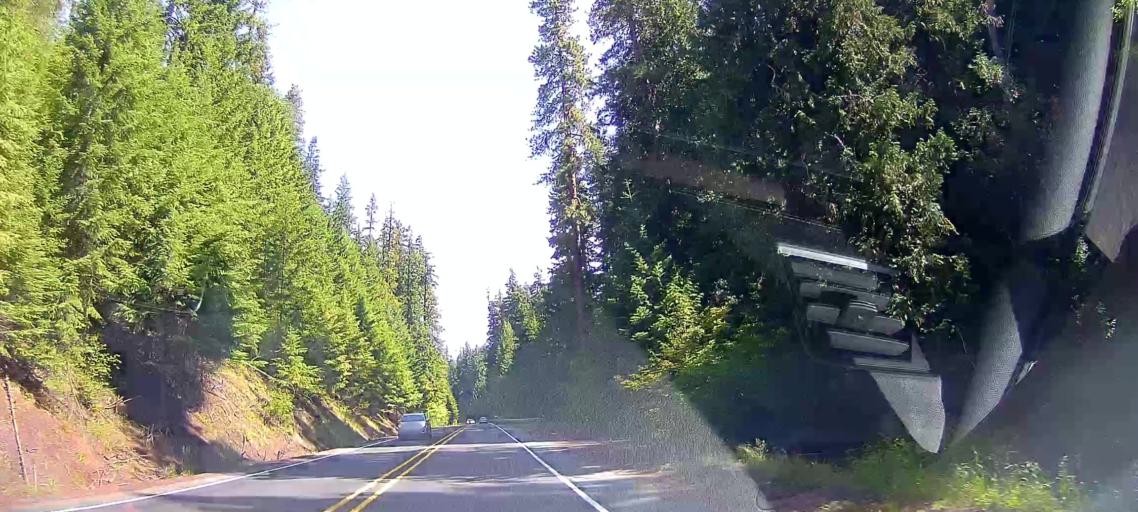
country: US
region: Oregon
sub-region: Jefferson County
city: Warm Springs
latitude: 45.0979
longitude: -121.5525
